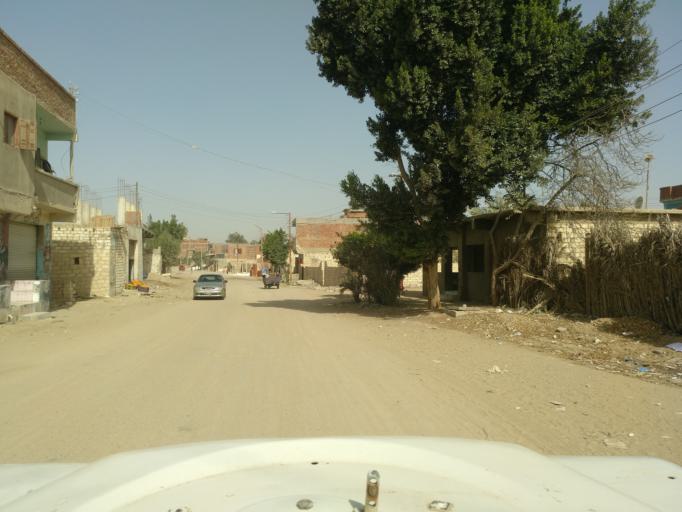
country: EG
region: Al Buhayrah
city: Beheira
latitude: 30.3804
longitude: 30.3451
